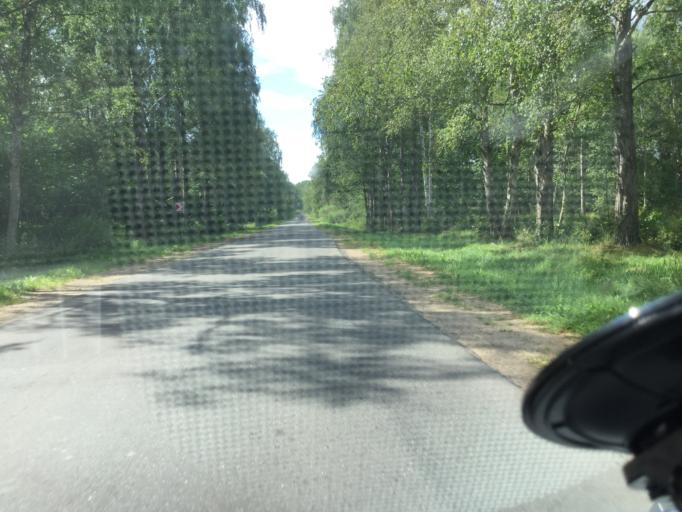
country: BY
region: Vitebsk
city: Chashniki
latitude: 55.3005
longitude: 29.3891
